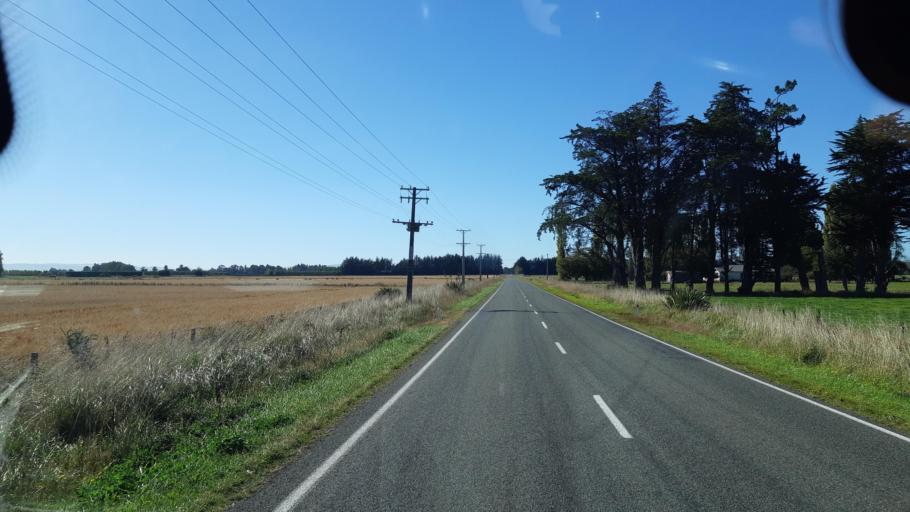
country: NZ
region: Southland
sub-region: Southland District
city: Winton
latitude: -46.1488
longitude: 168.2027
